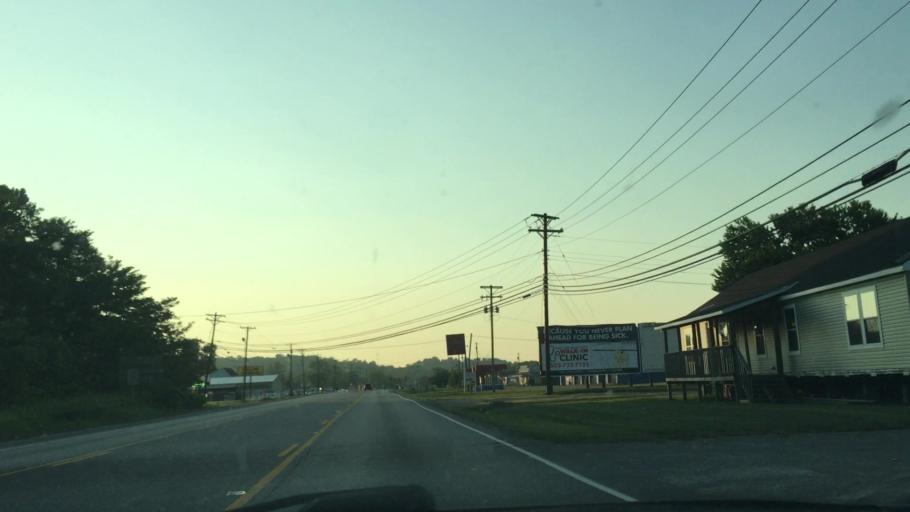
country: US
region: Kentucky
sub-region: Carroll County
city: Carrollton
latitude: 38.6602
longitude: -85.1380
